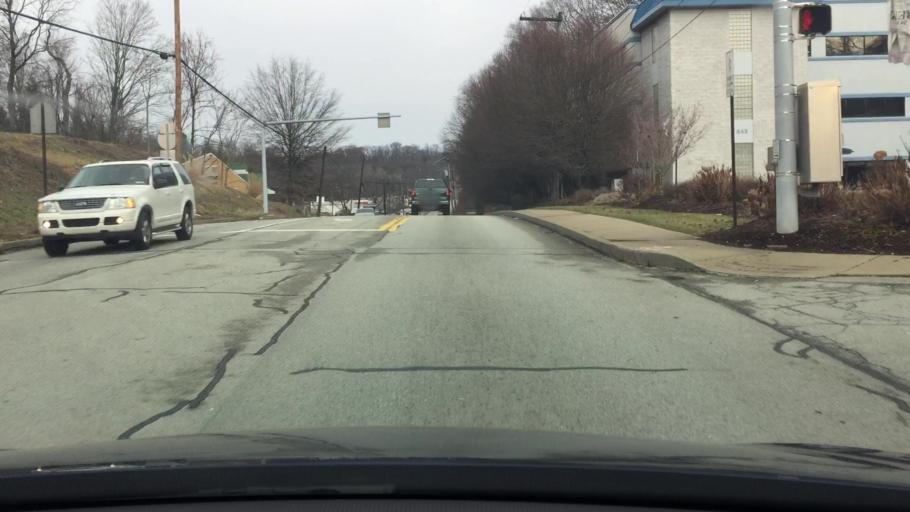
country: US
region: Pennsylvania
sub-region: Allegheny County
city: Churchill
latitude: 40.4460
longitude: -79.8279
